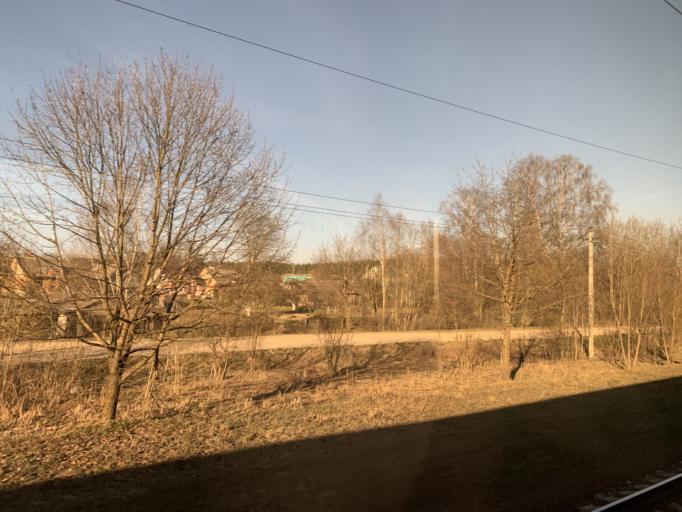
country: BY
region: Minsk
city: Pyatryshki
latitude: 54.1028
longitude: 27.1544
